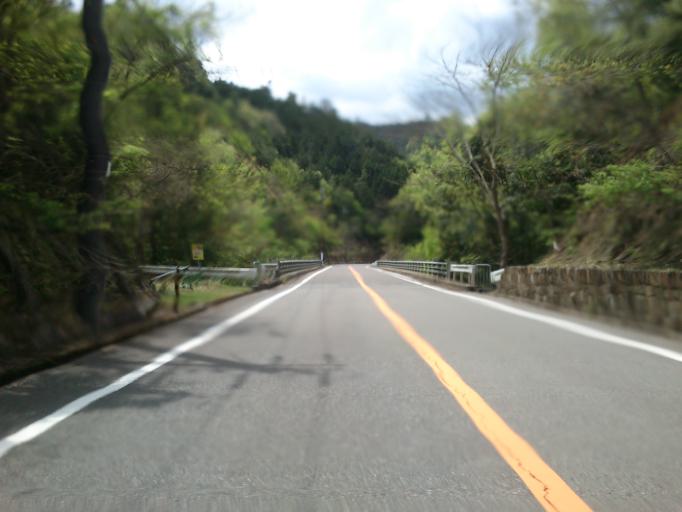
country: JP
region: Kyoto
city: Kameoka
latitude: 35.1308
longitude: 135.5473
